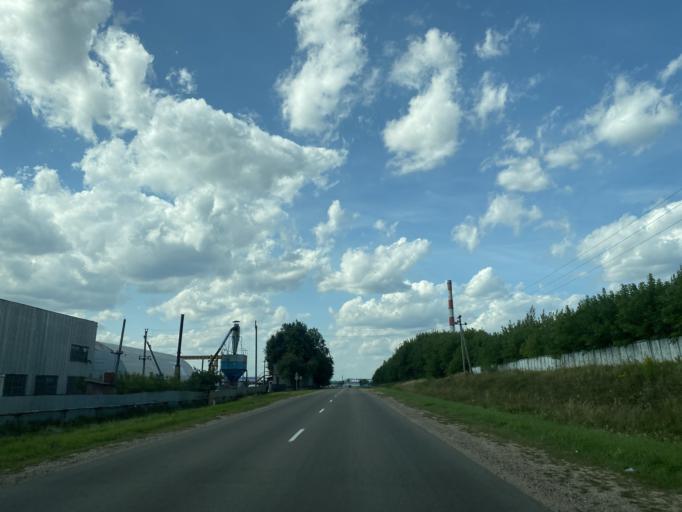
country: BY
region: Minsk
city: Horad Zhodzina
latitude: 54.0871
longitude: 28.3599
